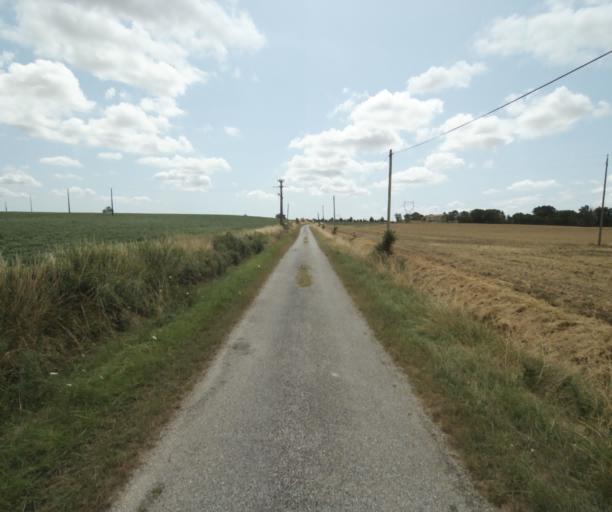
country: FR
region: Midi-Pyrenees
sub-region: Departement de la Haute-Garonne
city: Saint-Felix-Lauragais
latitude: 43.4195
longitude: 1.9041
